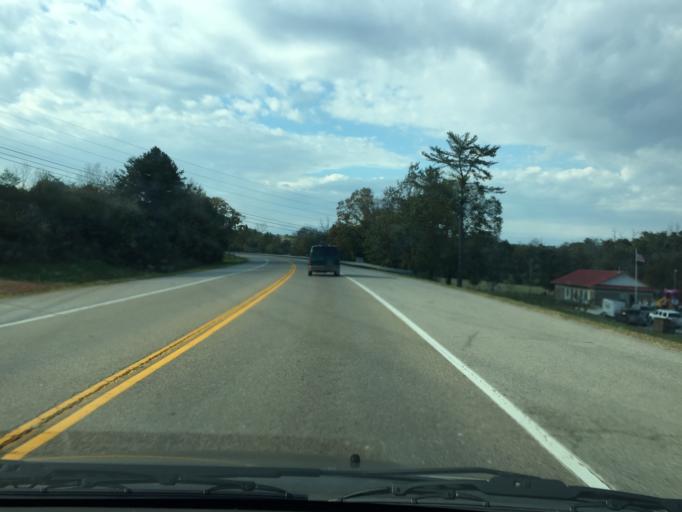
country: US
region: Tennessee
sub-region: Loudon County
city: Loudon
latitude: 35.7276
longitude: -84.3798
